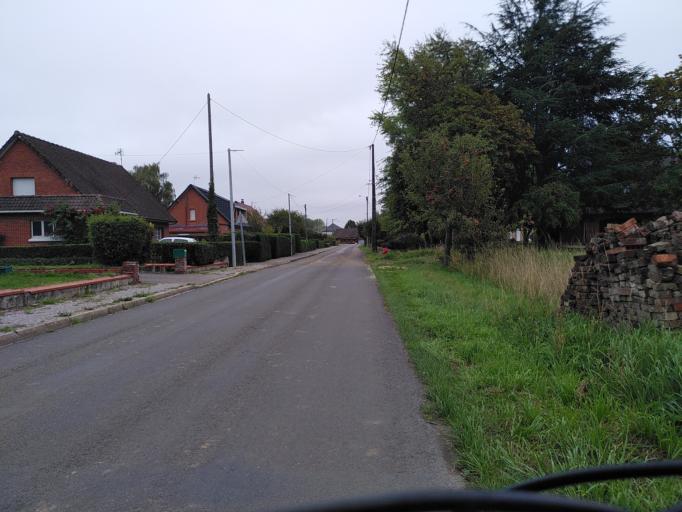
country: FR
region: Nord-Pas-de-Calais
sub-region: Departement du Pas-de-Calais
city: Saint-Venant
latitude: 50.6268
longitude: 2.5347
